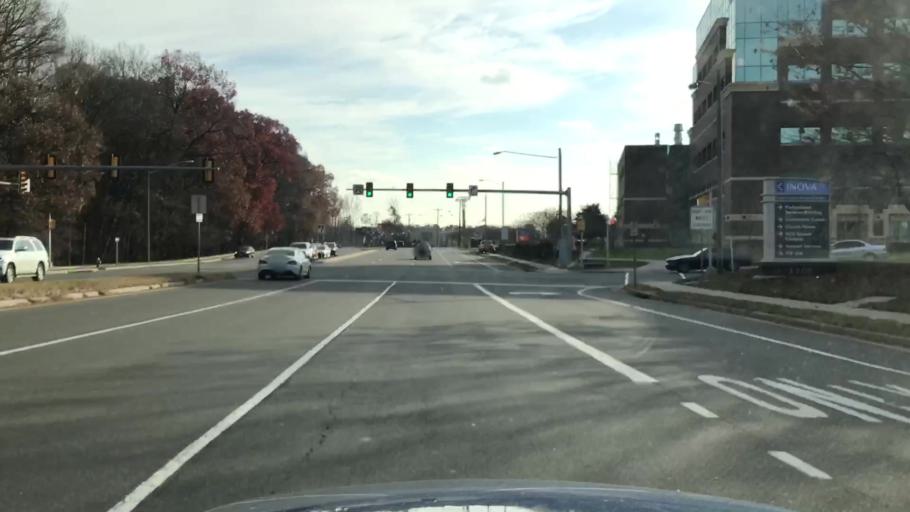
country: US
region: Virginia
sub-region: Fairfax County
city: Merrifield
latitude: 38.8593
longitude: -77.2262
